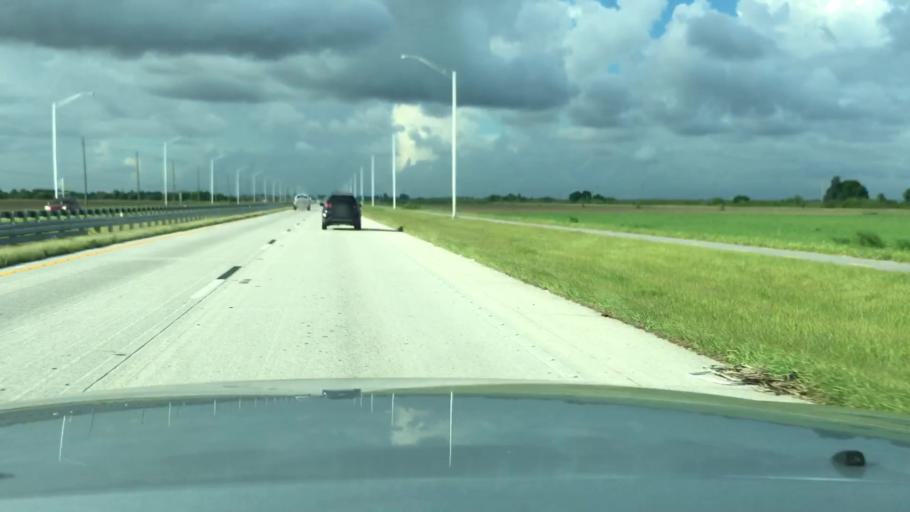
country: US
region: Florida
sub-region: Miami-Dade County
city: The Hammocks
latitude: 25.6520
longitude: -80.4802
